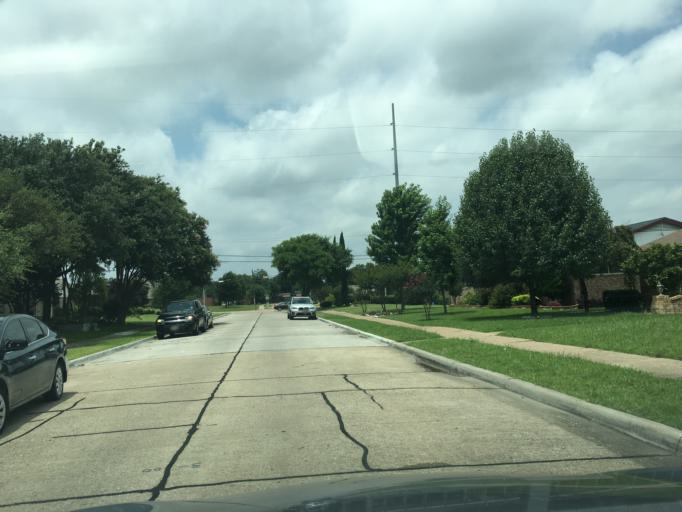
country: US
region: Texas
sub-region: Dallas County
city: Garland
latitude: 32.9260
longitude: -96.6818
